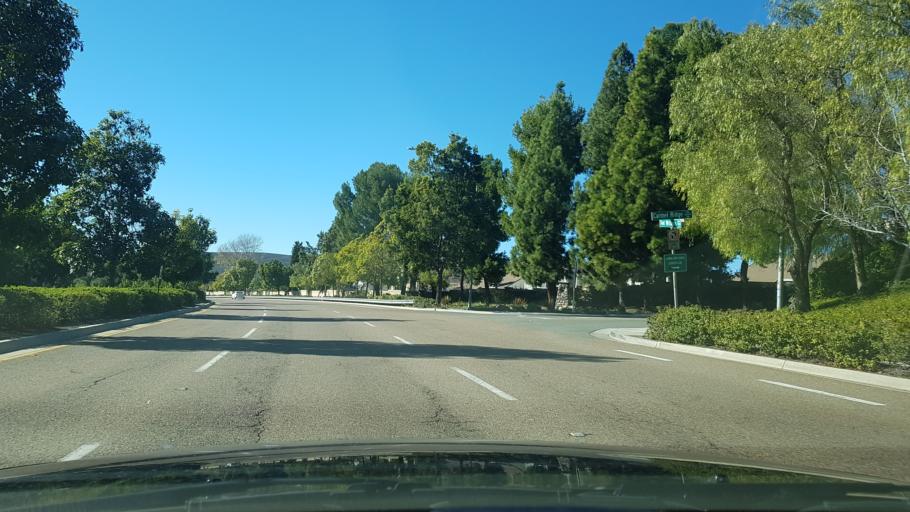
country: US
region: California
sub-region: San Diego County
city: Poway
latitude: 32.9715
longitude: -117.0769
